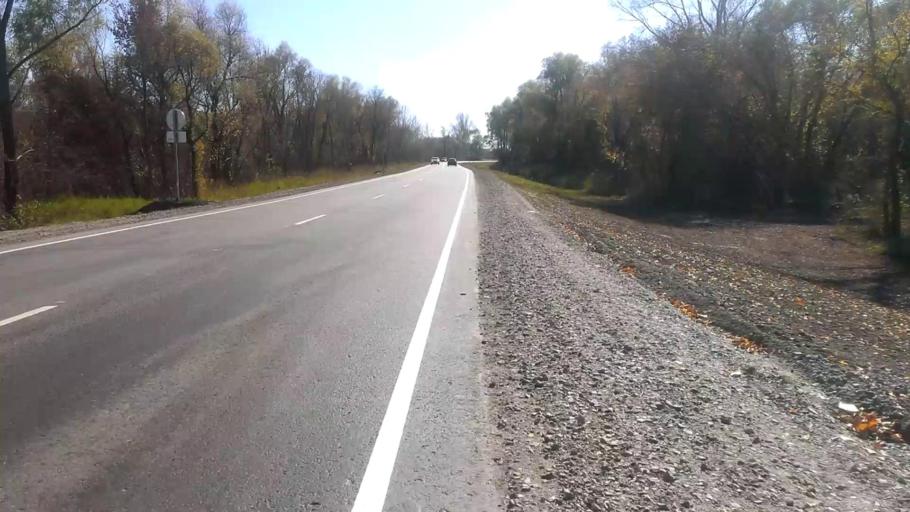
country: RU
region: Altai Krai
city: Sannikovo
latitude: 53.3260
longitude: 83.9419
